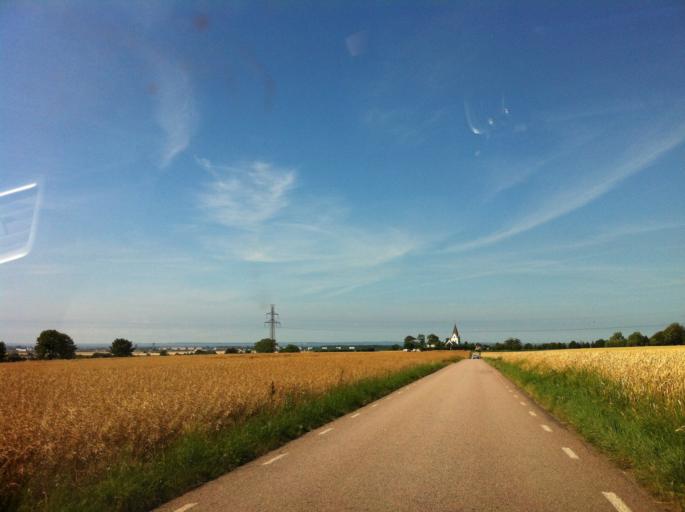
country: SE
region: Skane
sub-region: Landskrona
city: Asmundtorp
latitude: 55.9053
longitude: 12.9190
